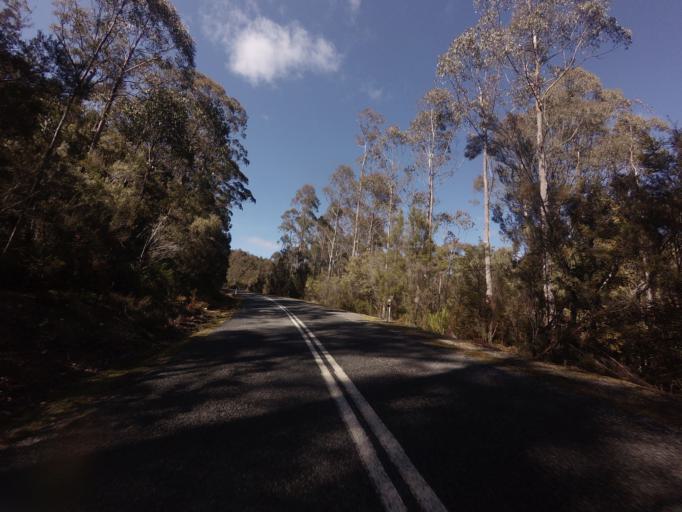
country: AU
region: Tasmania
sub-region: Huon Valley
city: Geeveston
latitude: -42.7799
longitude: 146.3983
